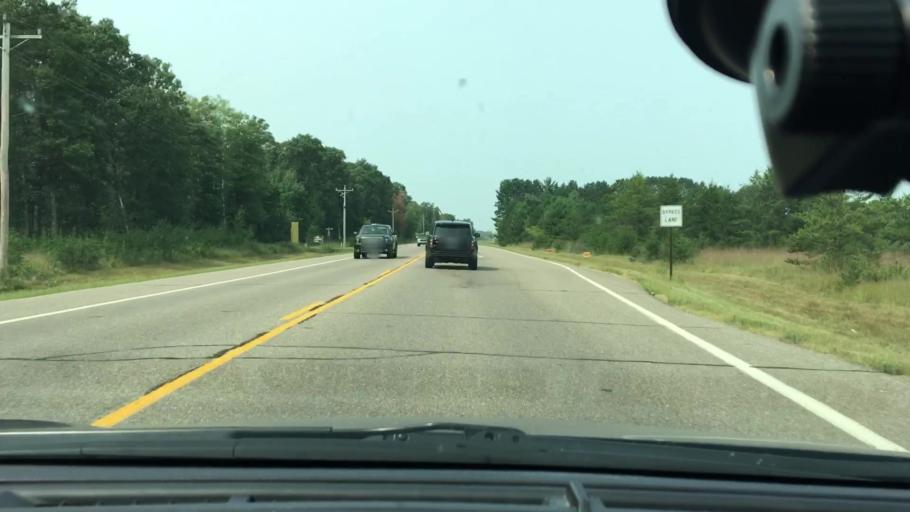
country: US
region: Minnesota
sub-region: Crow Wing County
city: Brainerd
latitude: 46.3984
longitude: -94.2036
